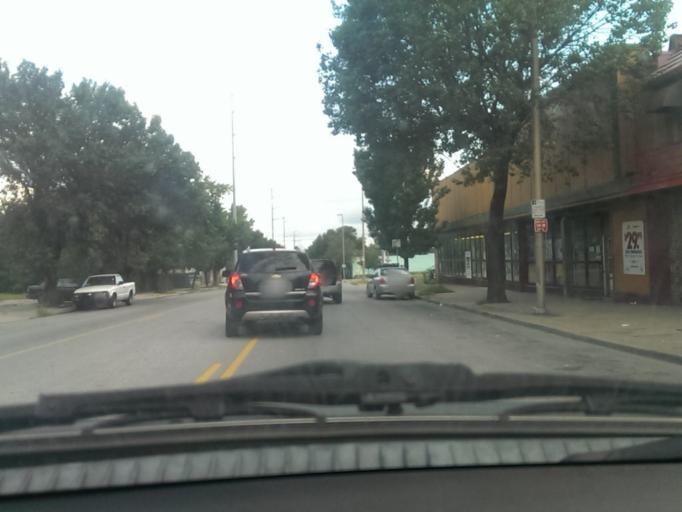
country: US
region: Missouri
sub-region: Jackson County
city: Kansas City
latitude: 39.0678
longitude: -94.5715
